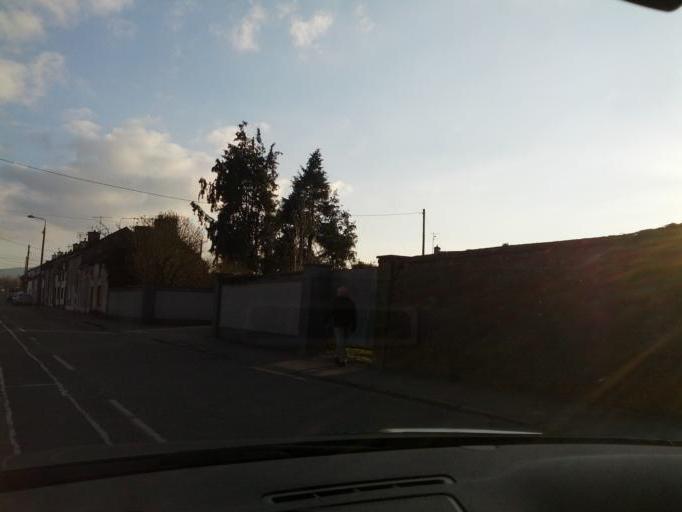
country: IE
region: Munster
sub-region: North Tipperary
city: Nenagh
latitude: 52.8596
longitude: -8.2034
